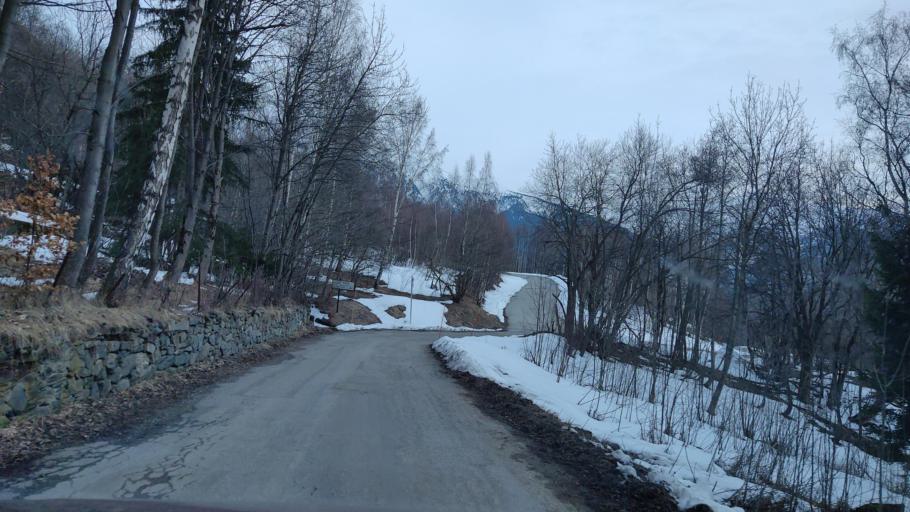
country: FR
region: Rhone-Alpes
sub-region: Departement de la Savoie
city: Saint-Michel-de-Maurienne
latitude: 45.2427
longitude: 6.4769
